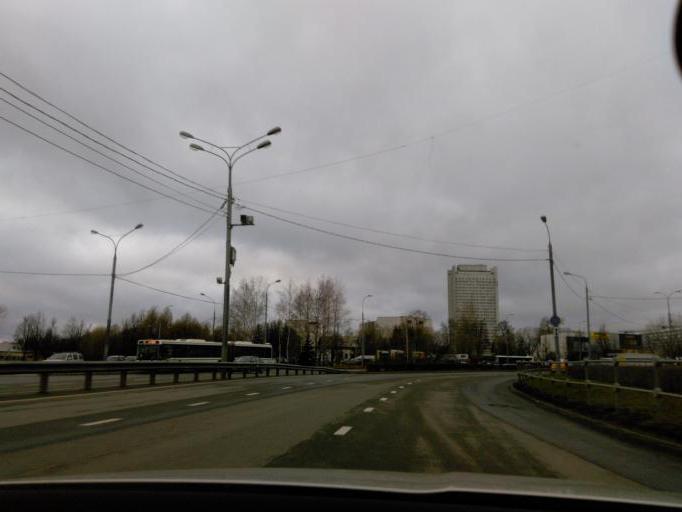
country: RU
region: Moskovskaya
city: Rzhavki
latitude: 55.9891
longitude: 37.2259
